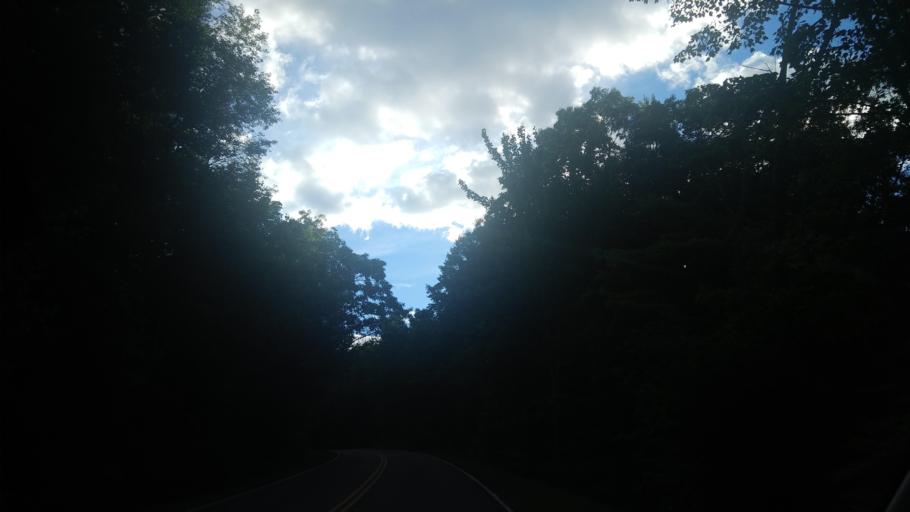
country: US
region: Tennessee
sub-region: Cocke County
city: Newport
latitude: 35.8141
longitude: -83.2211
